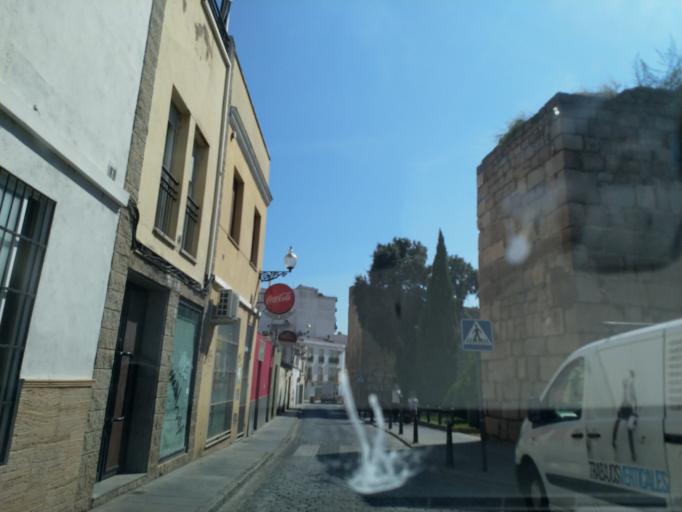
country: ES
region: Extremadura
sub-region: Provincia de Badajoz
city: Merida
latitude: 38.9153
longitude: -6.3460
